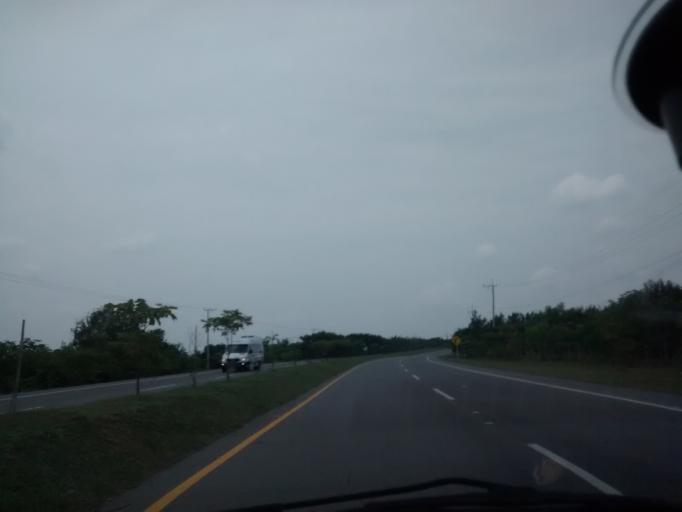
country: CO
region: Tolima
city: Espinal
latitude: 4.2362
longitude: -74.8960
